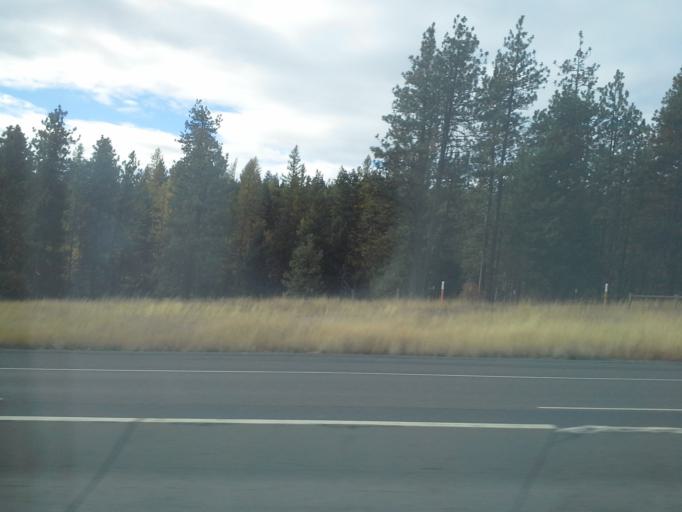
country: US
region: Oregon
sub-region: Union County
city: La Grande
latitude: 45.3920
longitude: -118.3240
